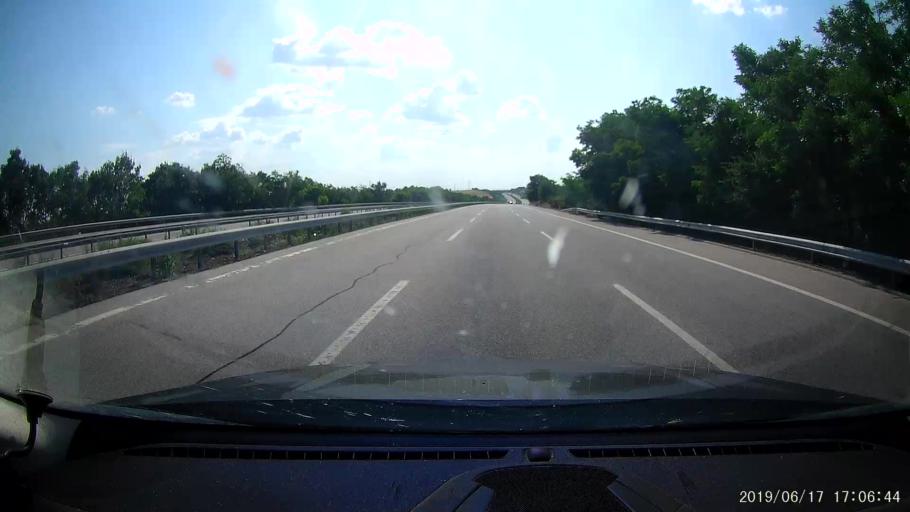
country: TR
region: Edirne
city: Edirne
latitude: 41.6616
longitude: 26.6618
